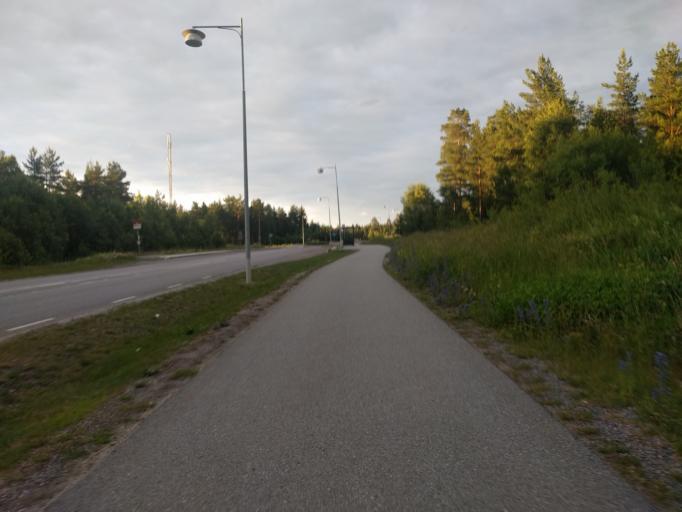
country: SE
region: Stockholm
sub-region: Vallentuna Kommun
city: Vallentuna
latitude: 59.5137
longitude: 18.0776
